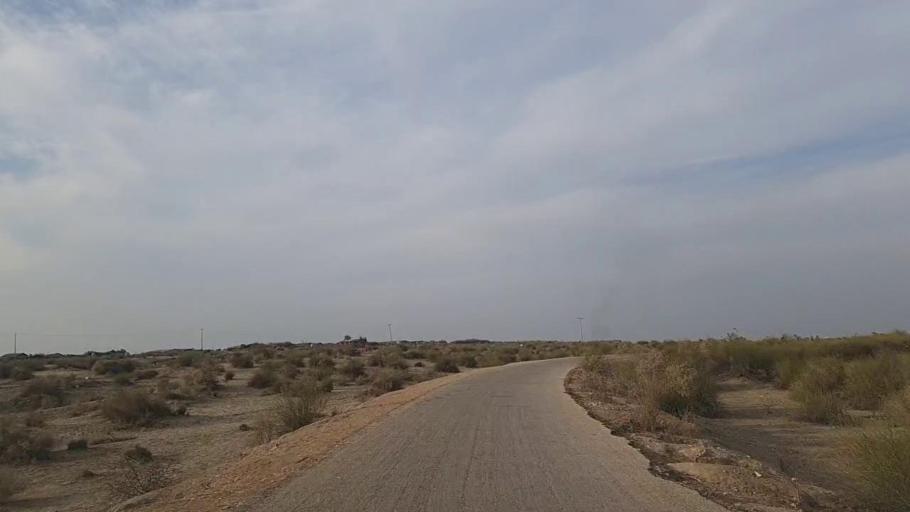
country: PK
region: Sindh
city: Daur
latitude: 26.5088
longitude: 68.4406
